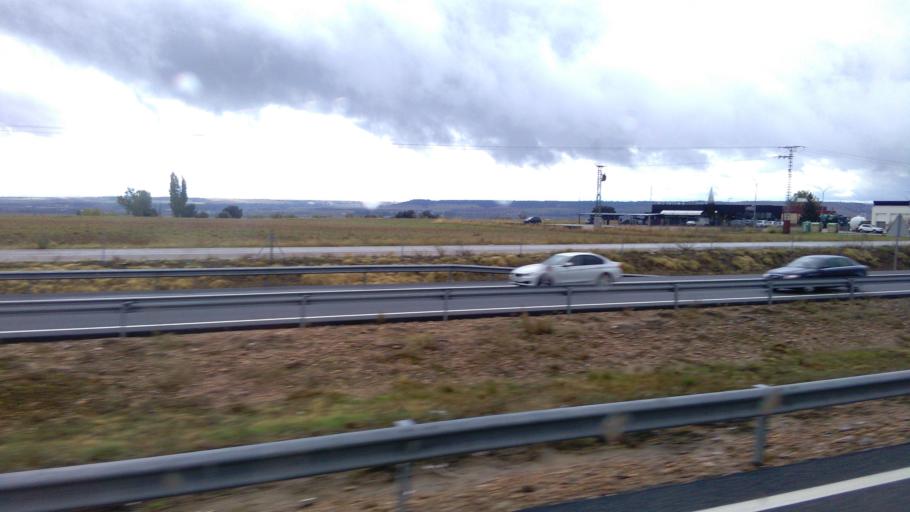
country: ES
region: Castille-La Mancha
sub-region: Province of Toledo
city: Cazalegas
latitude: 39.9899
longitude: -4.7023
